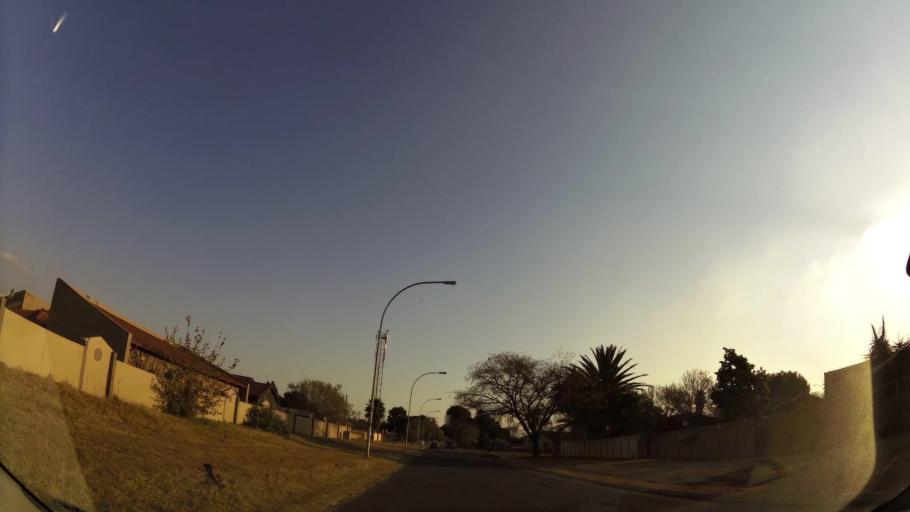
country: ZA
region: Gauteng
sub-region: Ekurhuleni Metropolitan Municipality
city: Benoni
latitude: -26.1227
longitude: 28.3745
